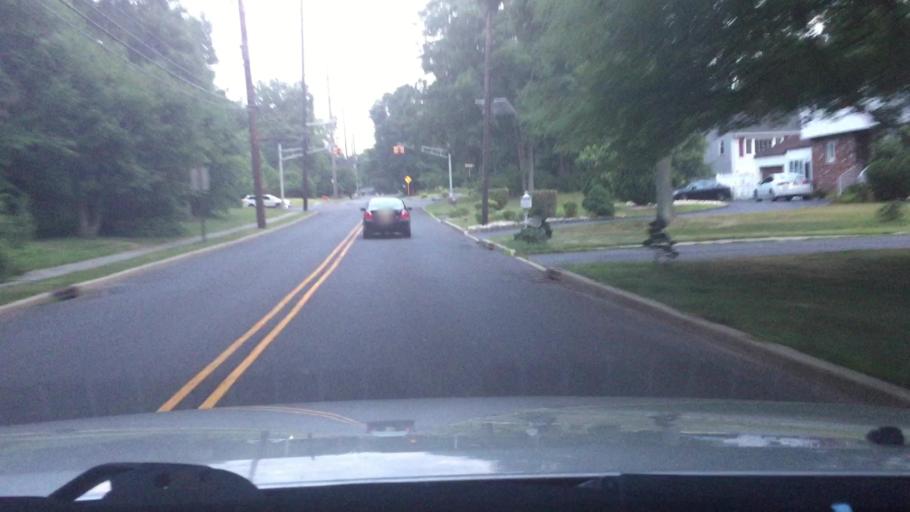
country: US
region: New Jersey
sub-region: Middlesex County
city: Milltown
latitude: 40.4303
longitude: -74.4519
